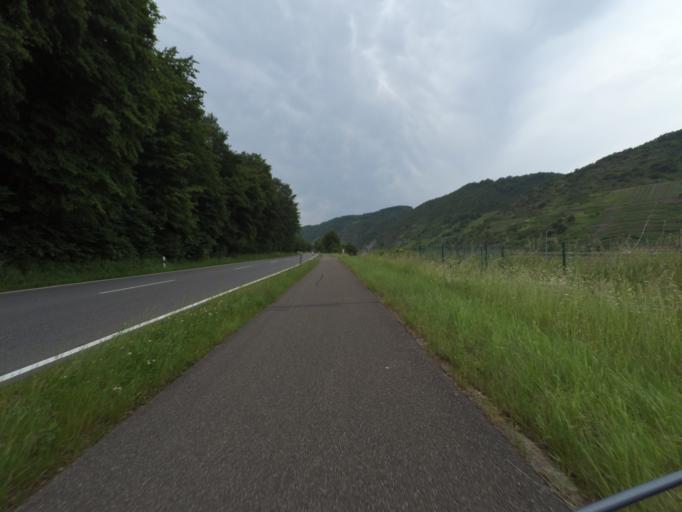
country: DE
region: Rheinland-Pfalz
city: Lutz
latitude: 50.1830
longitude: 7.3282
